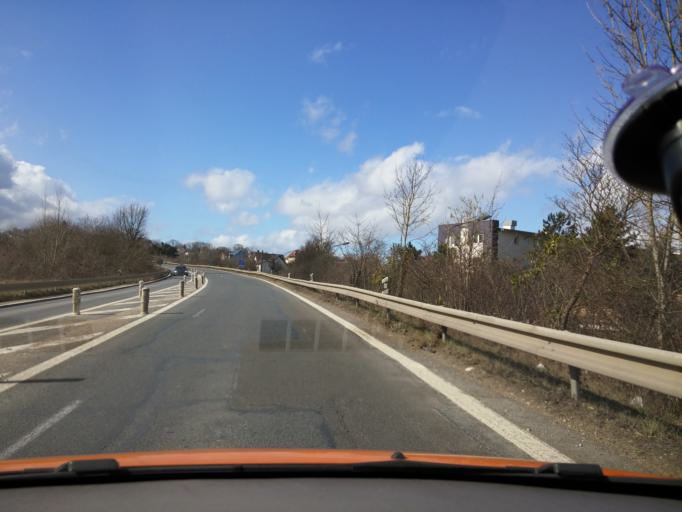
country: FR
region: Ile-de-France
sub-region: Departement de l'Essonne
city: Palaiseau
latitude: 48.7245
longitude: 2.2435
